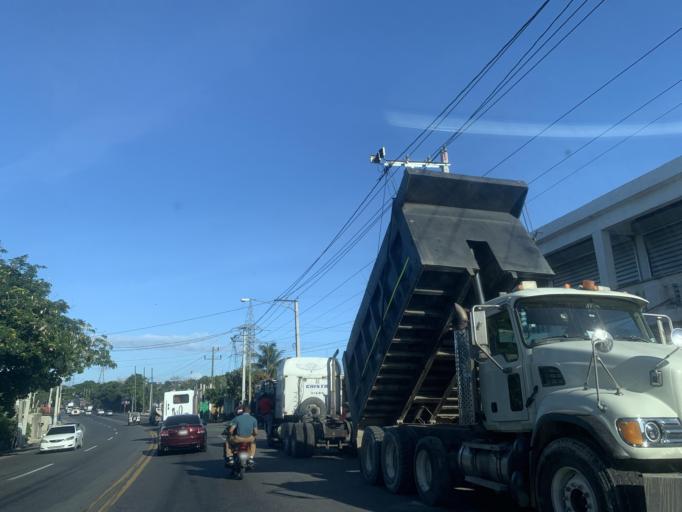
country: DO
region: San Cristobal
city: El Carril
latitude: 18.4331
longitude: -70.0096
